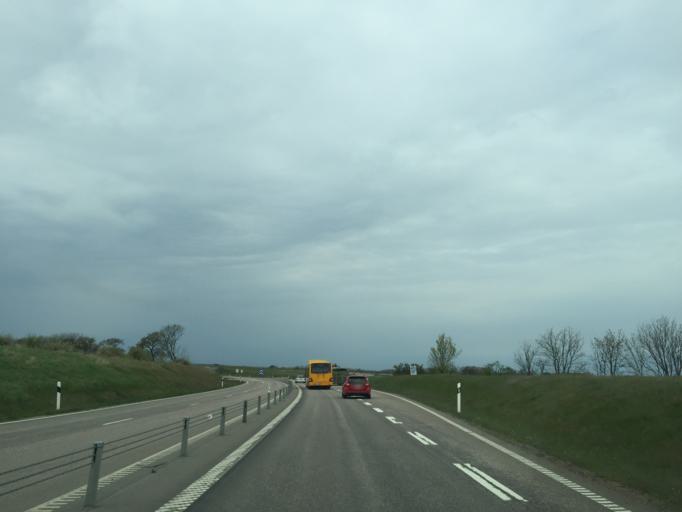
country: SE
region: Skane
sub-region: Hoganas Kommun
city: Hoganas
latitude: 56.1613
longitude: 12.5901
